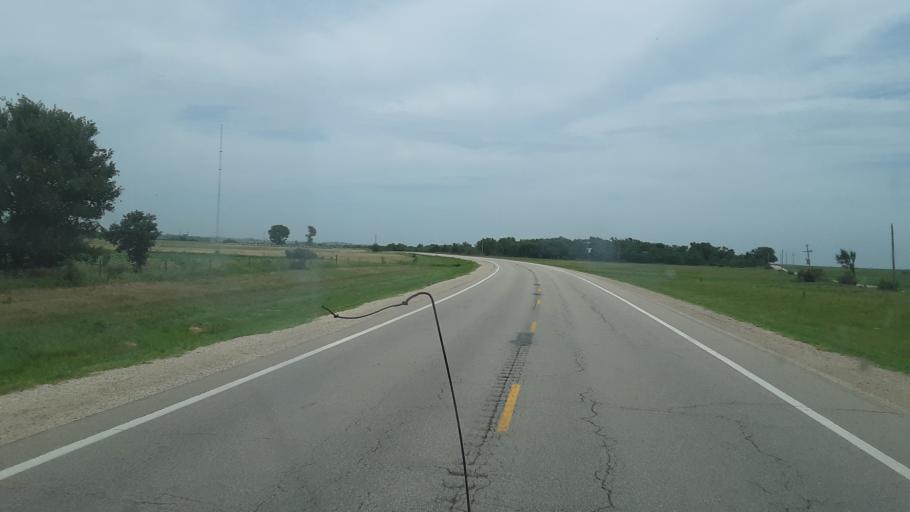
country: US
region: Kansas
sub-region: Woodson County
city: Yates Center
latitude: 37.8366
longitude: -95.8527
